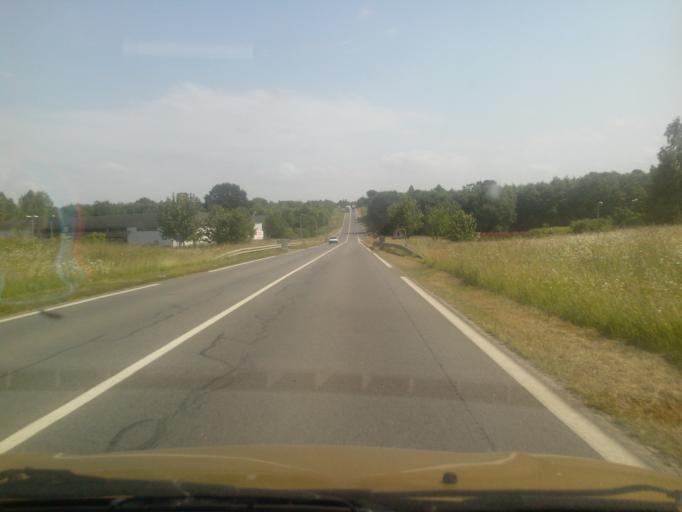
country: FR
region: Brittany
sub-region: Departement d'Ille-et-Vilaine
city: Melesse
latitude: 48.2136
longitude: -1.7011
